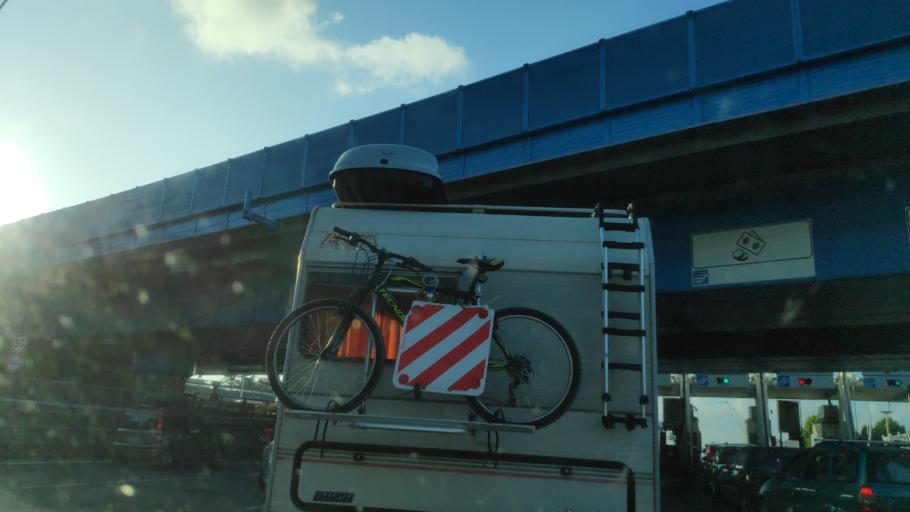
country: IT
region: Campania
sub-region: Provincia di Napoli
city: Casavatore
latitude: 40.8701
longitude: 14.2731
